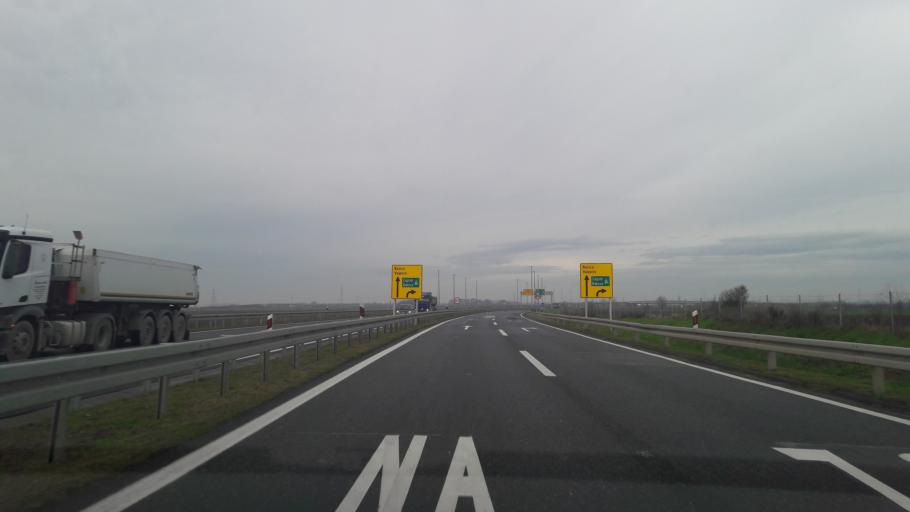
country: HR
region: Osjecko-Baranjska
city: Josipovac
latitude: 45.5715
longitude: 18.5774
